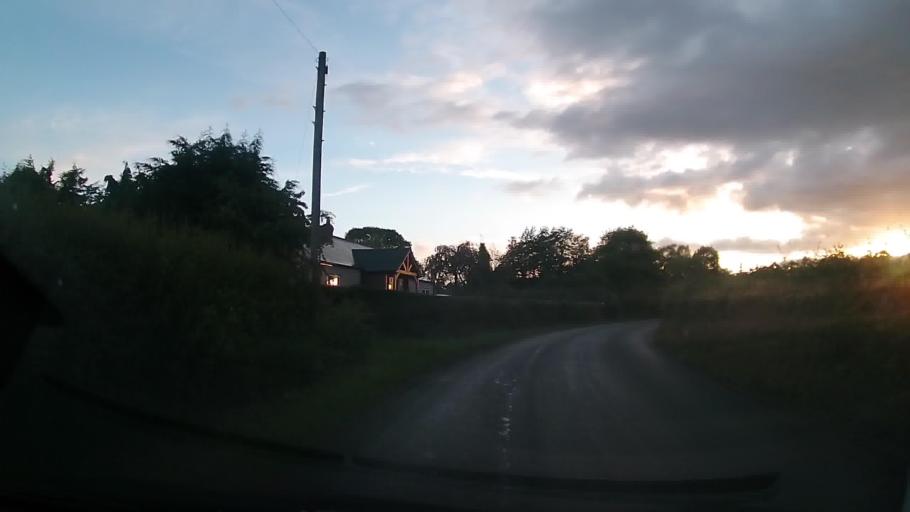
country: GB
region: England
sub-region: Shropshire
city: Prees
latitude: 52.8954
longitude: -2.6518
